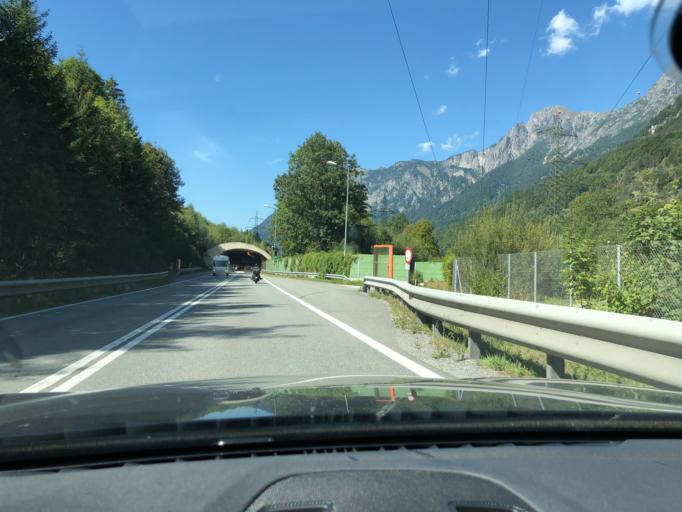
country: AT
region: Vorarlberg
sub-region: Politischer Bezirk Bludenz
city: Innerbraz
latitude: 47.1352
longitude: 9.9424
